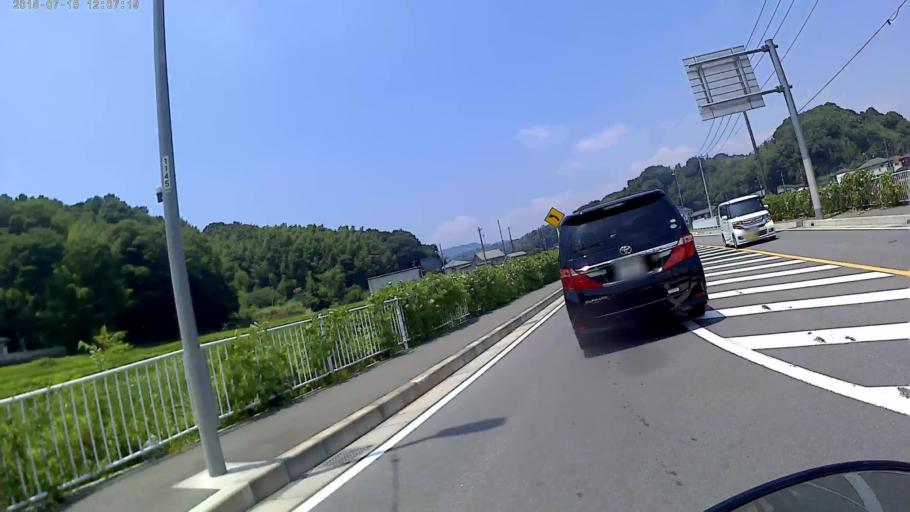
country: JP
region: Kanagawa
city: Hadano
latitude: 35.3304
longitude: 139.2169
